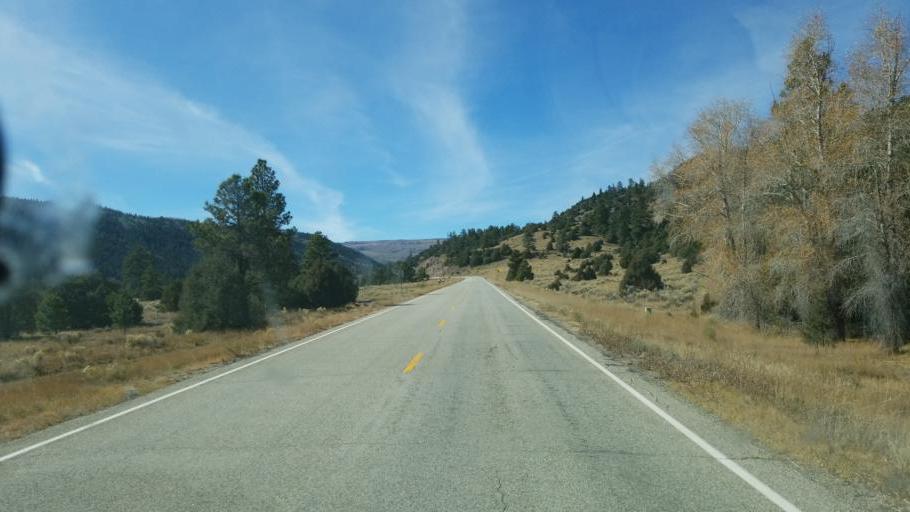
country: US
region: Colorado
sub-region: Conejos County
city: Conejos
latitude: 37.0684
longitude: -106.2381
